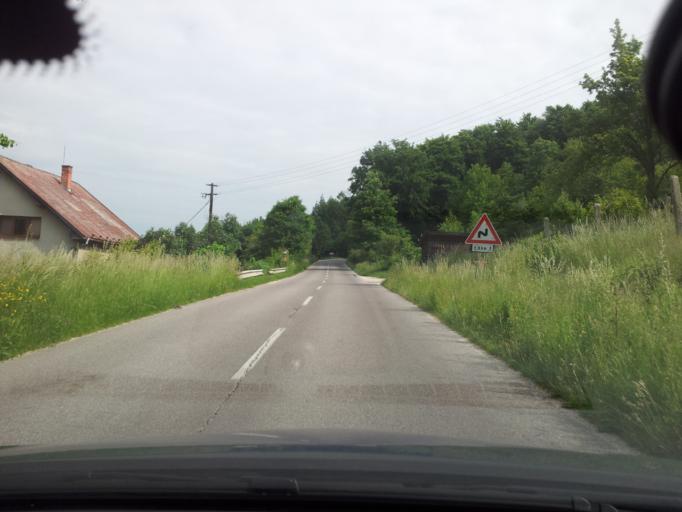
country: SK
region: Nitriansky
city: Partizanske
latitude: 48.5291
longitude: 18.4404
